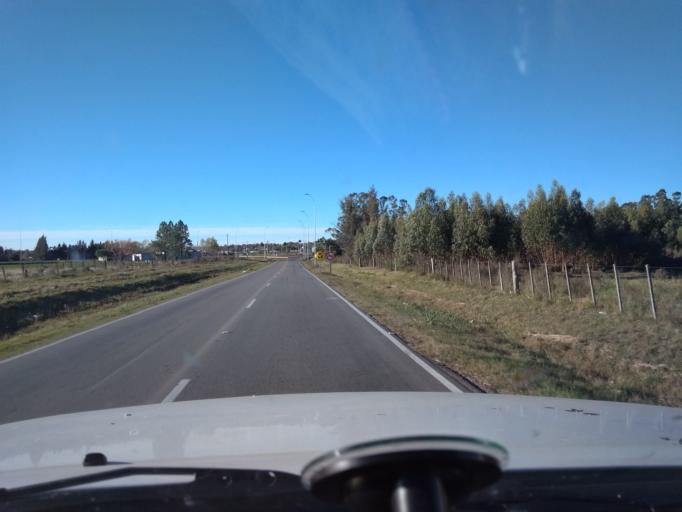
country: UY
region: Canelones
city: Santa Rosa
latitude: -34.5070
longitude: -56.0508
